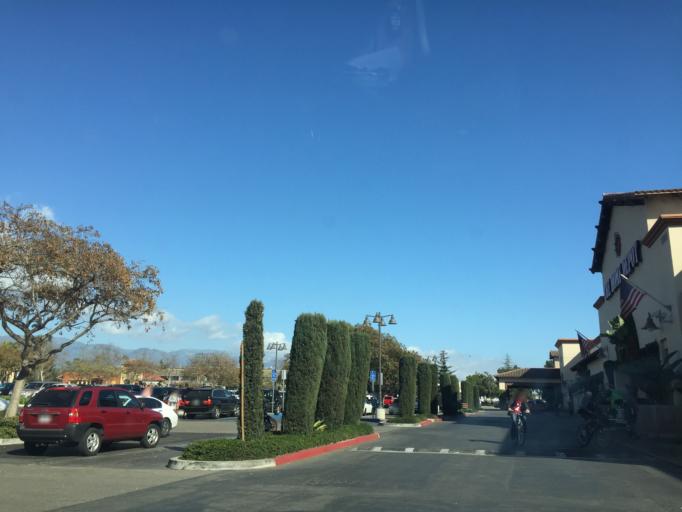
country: US
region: California
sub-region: Santa Barbara County
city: Isla Vista
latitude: 34.4280
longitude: -119.8716
